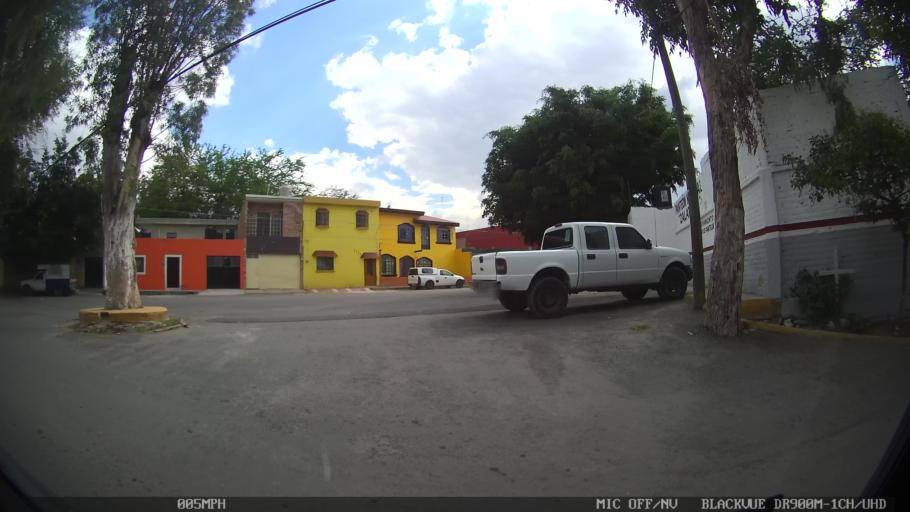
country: MX
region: Jalisco
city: Tlaquepaque
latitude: 20.6631
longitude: -103.2636
